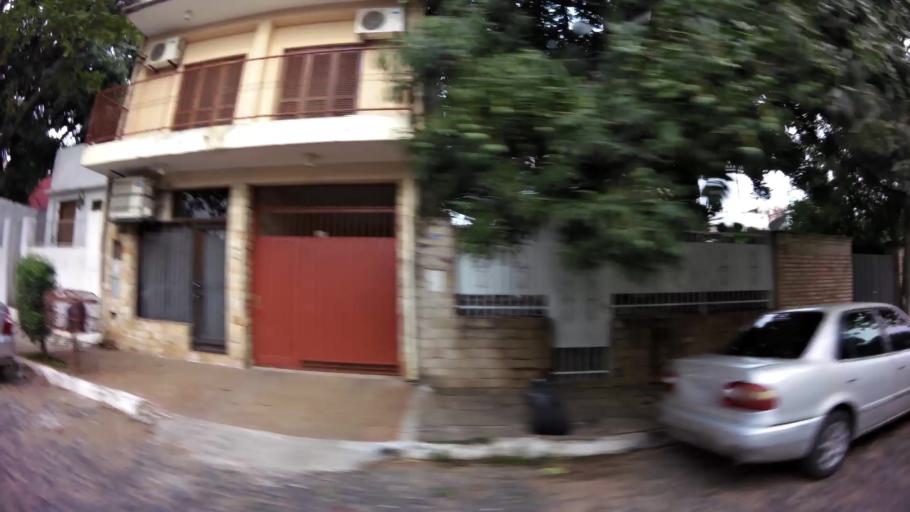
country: PY
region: Asuncion
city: Asuncion
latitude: -25.3073
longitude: -57.6135
